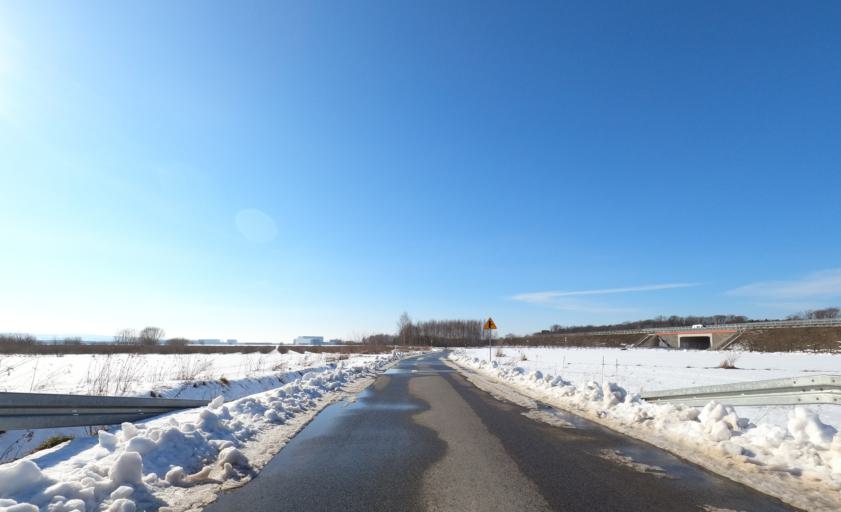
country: PL
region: Subcarpathian Voivodeship
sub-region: Powiat debicki
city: Brzeznica
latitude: 50.0805
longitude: 21.4862
